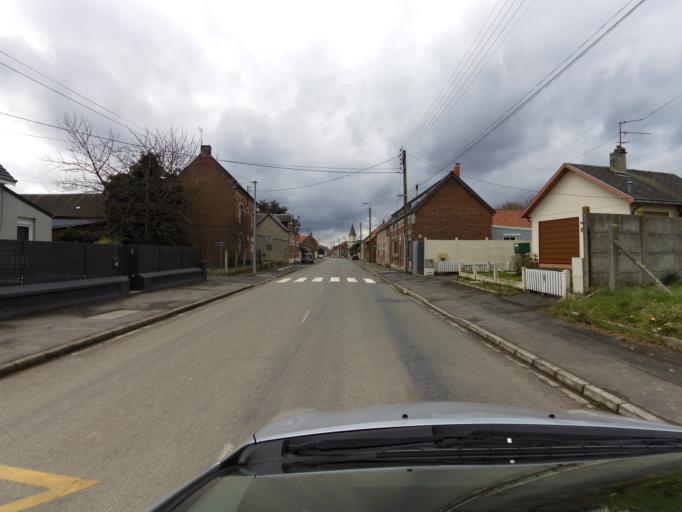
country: FR
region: Nord-Pas-de-Calais
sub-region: Departement du Pas-de-Calais
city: Beaurains
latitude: 50.2361
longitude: 2.7989
